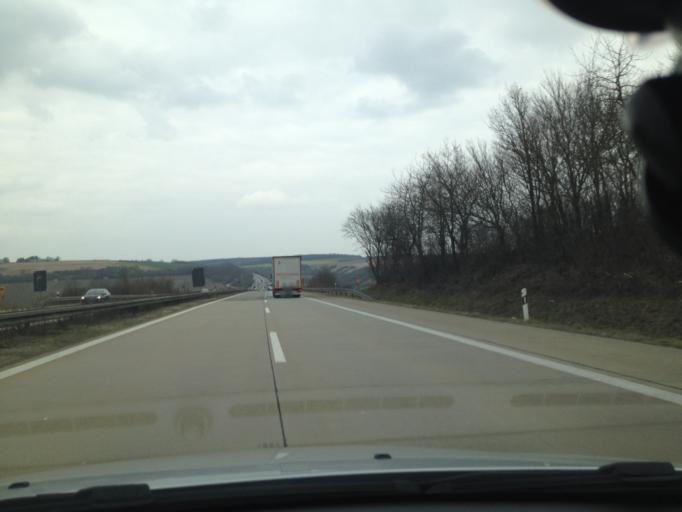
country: DE
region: Bavaria
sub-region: Regierungsbezirk Unterfranken
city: Segnitz
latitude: 49.6627
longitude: 10.1302
